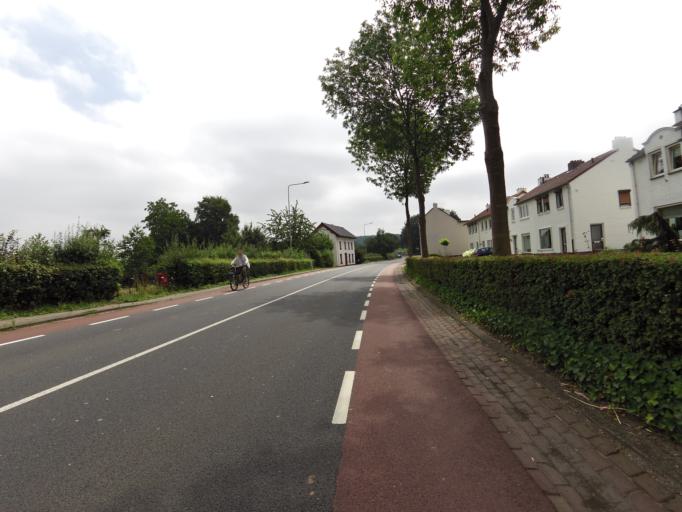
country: NL
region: Limburg
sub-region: Valkenburg aan de Geul
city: Schin op Geul
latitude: 50.8539
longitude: 5.8565
